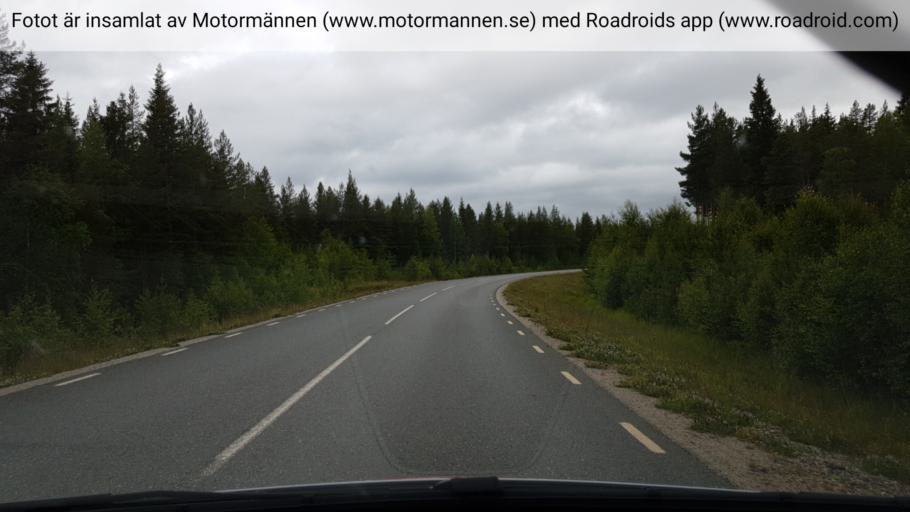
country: SE
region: Vaesterbotten
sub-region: Lycksele Kommun
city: Lycksele
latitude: 64.5126
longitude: 18.9873
